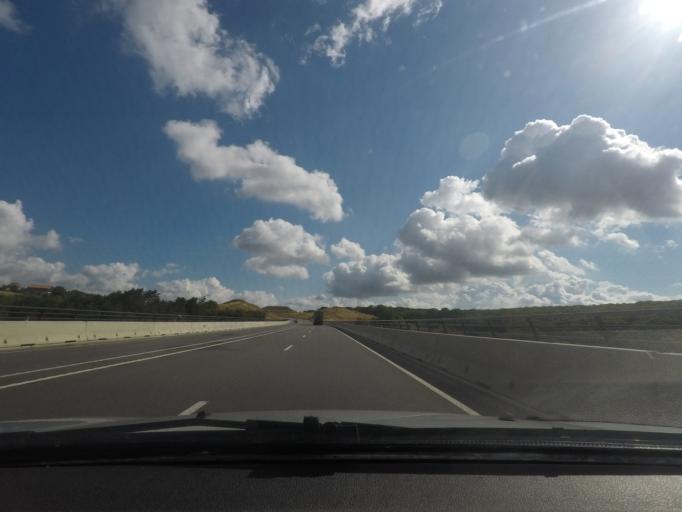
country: LU
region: Grevenmacher
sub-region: Canton de Grevenmacher
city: Junglinster
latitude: 49.7038
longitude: 6.2585
